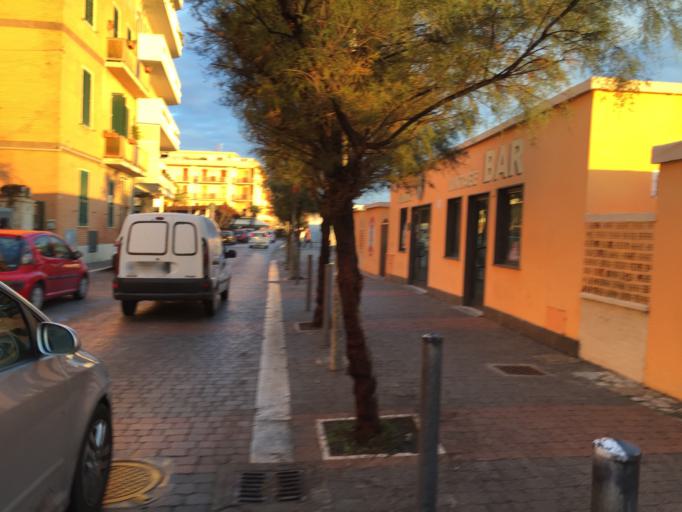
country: IT
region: Latium
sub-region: Citta metropolitana di Roma Capitale
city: Ladispoli
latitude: 41.9480
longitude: 12.0760
